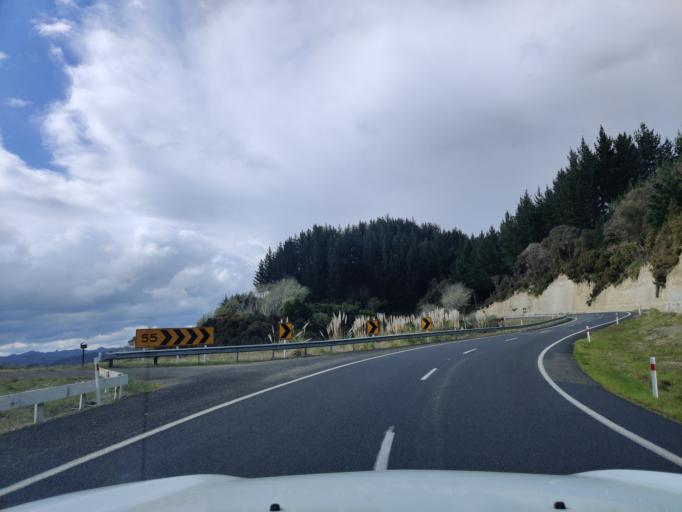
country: NZ
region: Manawatu-Wanganui
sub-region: Wanganui District
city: Wanganui
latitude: -39.7988
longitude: 175.1975
